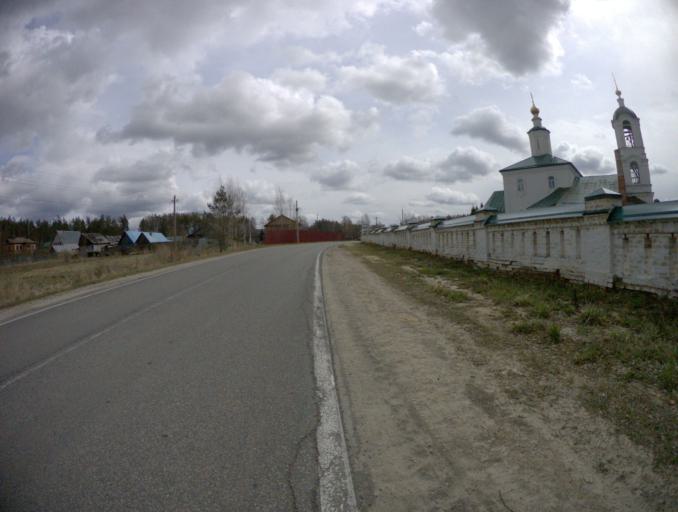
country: RU
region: Vladimir
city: Sudogda
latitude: 56.0736
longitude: 40.7857
